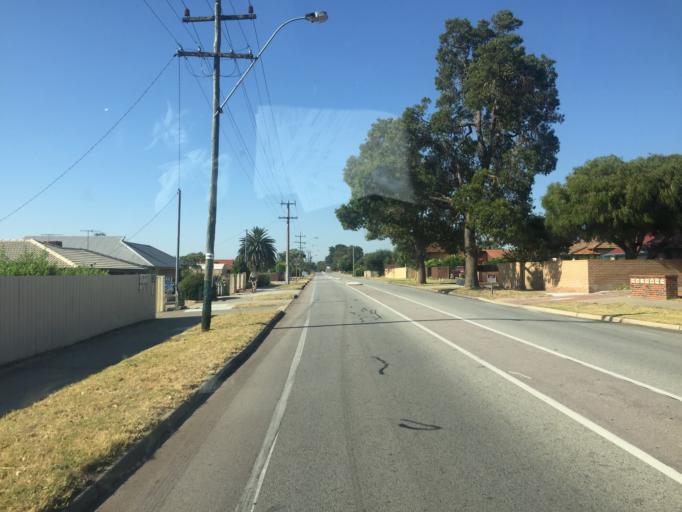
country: AU
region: Western Australia
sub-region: Gosnells
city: Maddington
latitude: -32.0397
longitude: 115.9820
